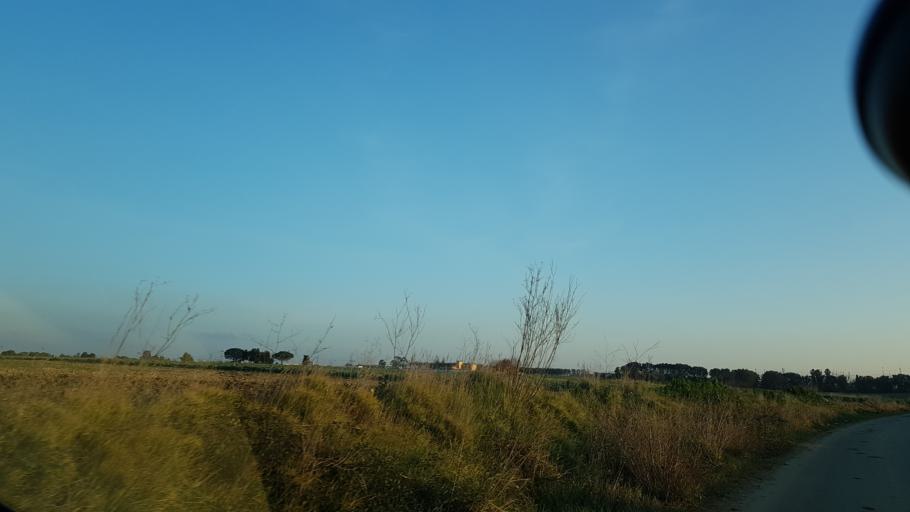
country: IT
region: Apulia
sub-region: Provincia di Brindisi
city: La Rosa
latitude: 40.6152
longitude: 17.9403
